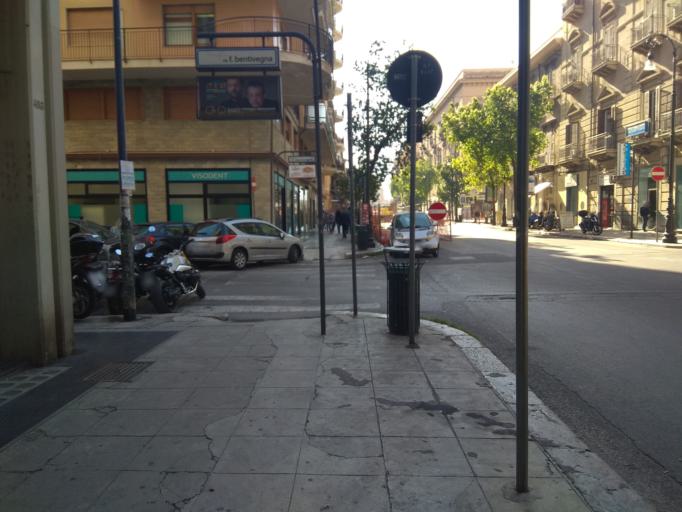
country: IT
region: Sicily
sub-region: Palermo
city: Palermo
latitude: 38.1232
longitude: 13.3601
